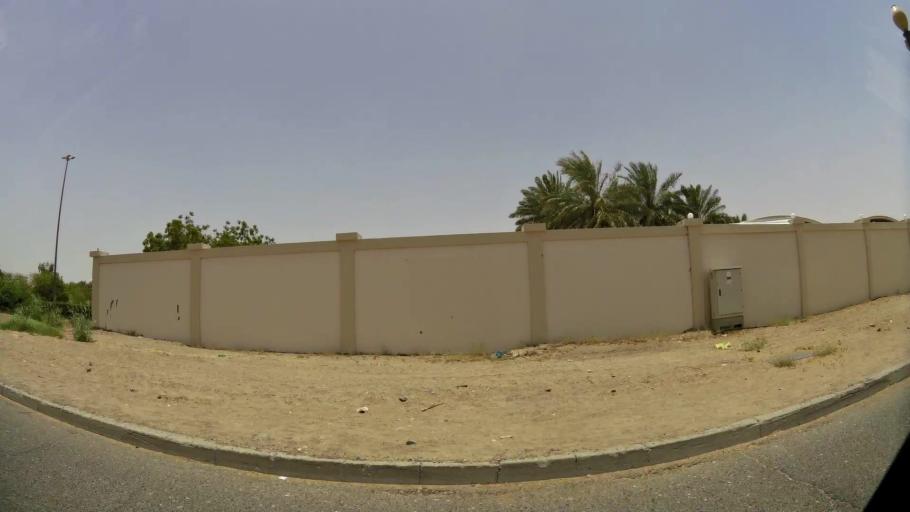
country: AE
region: Abu Dhabi
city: Al Ain
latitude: 24.2208
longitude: 55.7321
